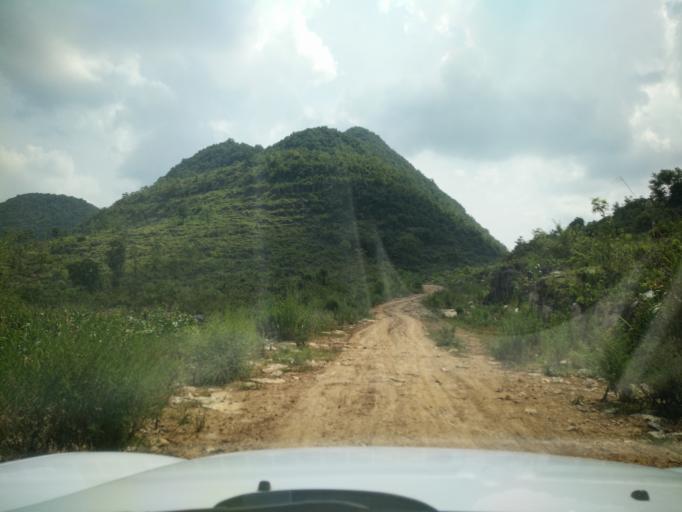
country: CN
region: Guangxi Zhuangzu Zizhiqu
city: Xinzhou
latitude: 25.1326
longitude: 105.6636
